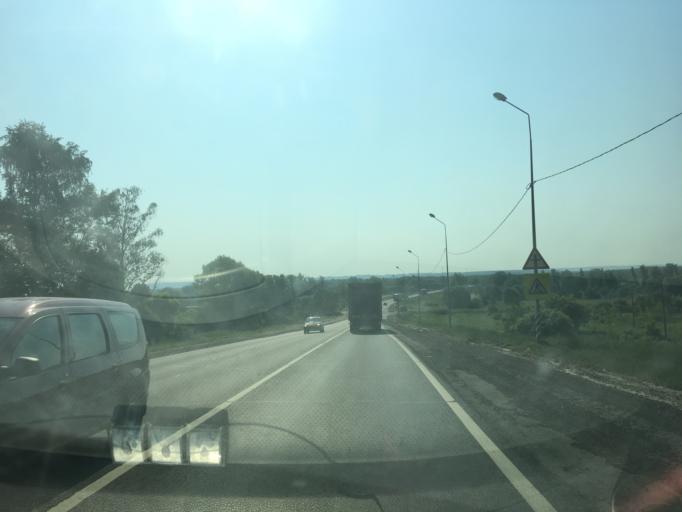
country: RU
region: Nizjnij Novgorod
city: Kstovo
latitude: 56.1009
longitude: 44.3031
